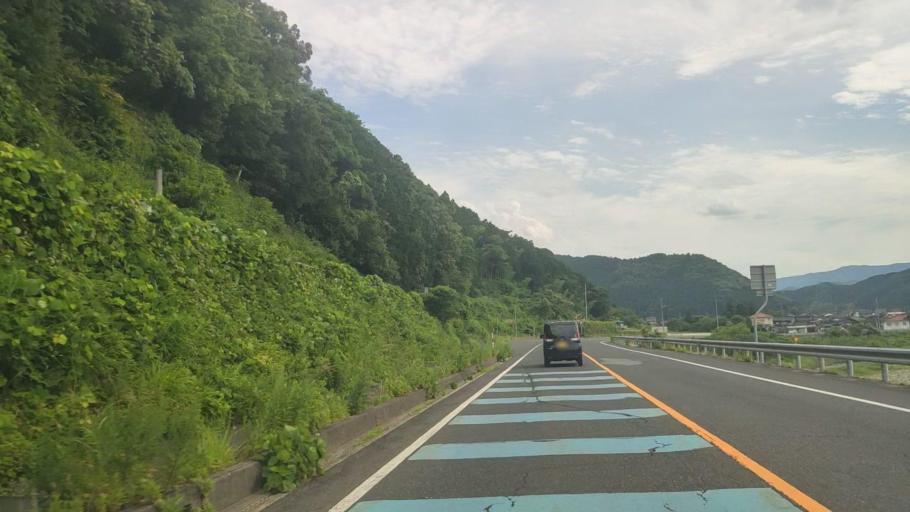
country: JP
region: Tottori
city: Tottori
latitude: 35.3623
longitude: 134.2132
